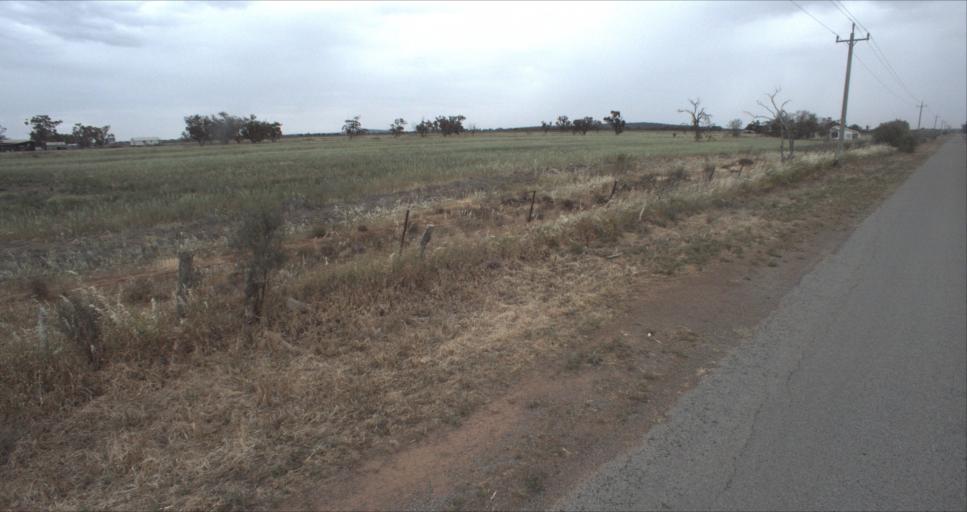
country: AU
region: New South Wales
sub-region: Leeton
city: Leeton
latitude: -34.4139
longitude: 146.3398
